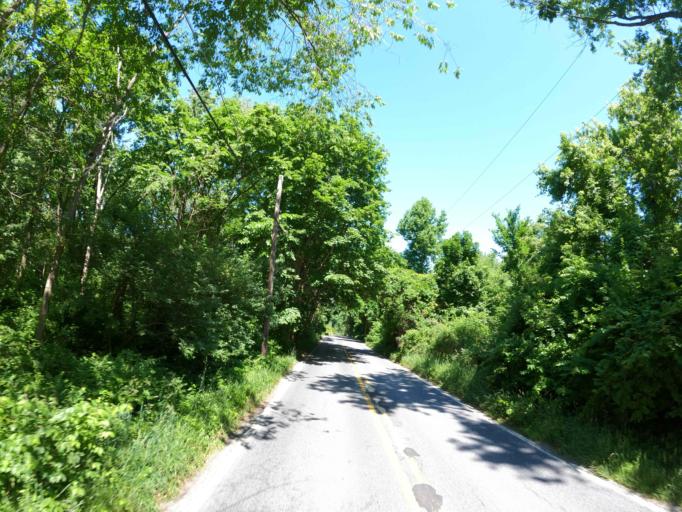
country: US
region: Maryland
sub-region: Montgomery County
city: Clarksburg
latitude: 39.2610
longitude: -77.2801
